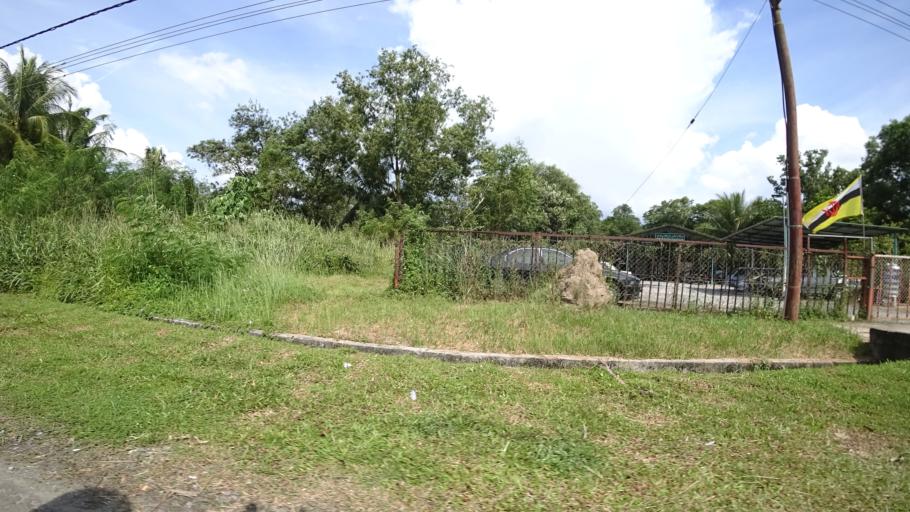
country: BN
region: Brunei and Muara
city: Bandar Seri Begawan
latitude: 4.8488
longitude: 114.8881
